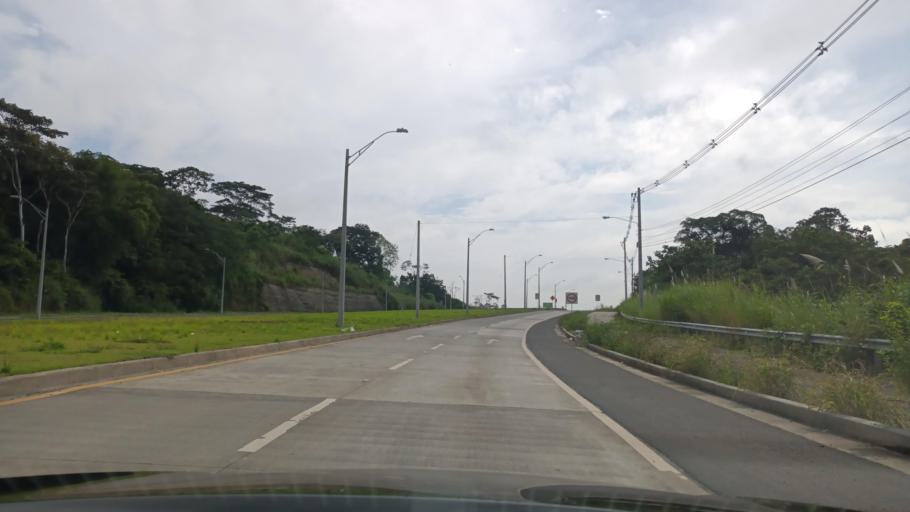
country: PA
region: Panama
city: Las Cumbres
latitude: 9.1042
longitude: -79.5281
